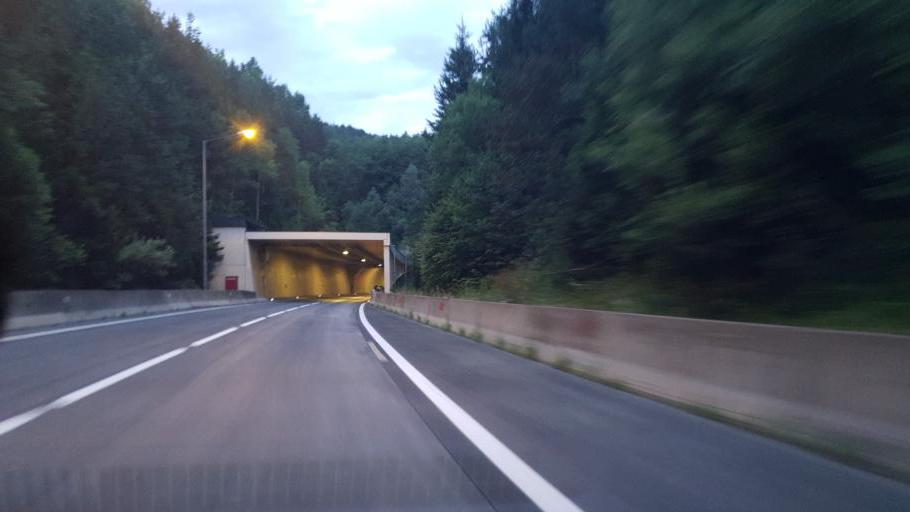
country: AT
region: Carinthia
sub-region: Politischer Bezirk Spittal an der Drau
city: Seeboden
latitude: 46.8056
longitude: 13.5200
